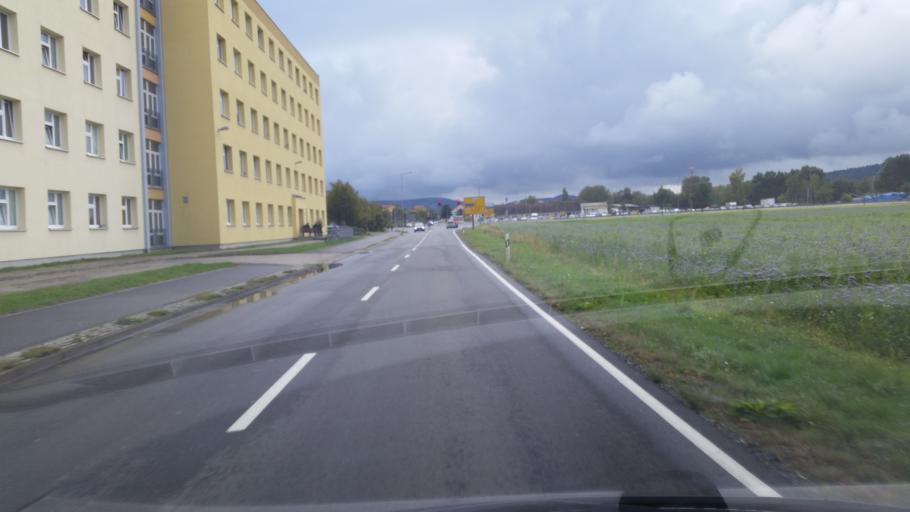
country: DE
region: Saxony
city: Kamenz
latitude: 51.2927
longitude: 14.1141
